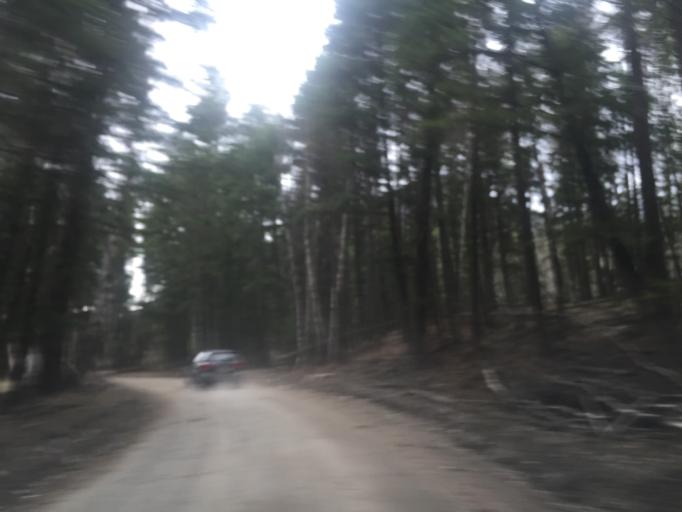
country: CA
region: British Columbia
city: Chase
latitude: 51.4010
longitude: -120.1246
